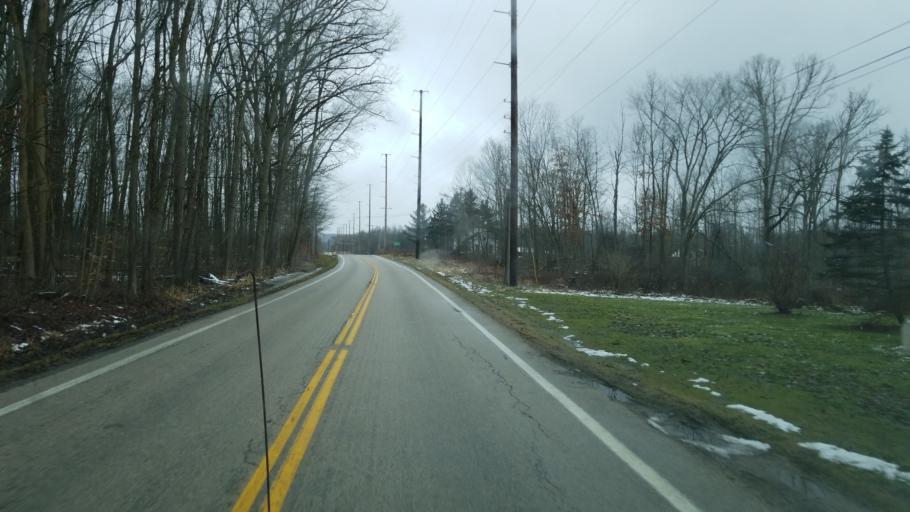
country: US
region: Ohio
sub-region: Portage County
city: Windham
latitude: 41.3098
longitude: -81.0017
